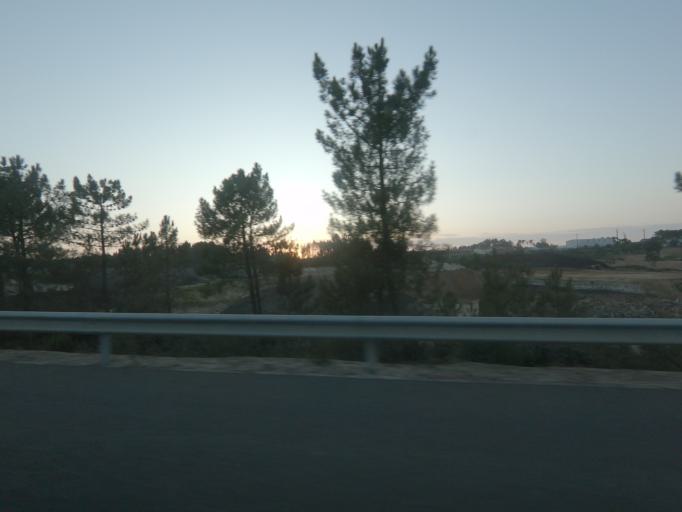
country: PT
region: Leiria
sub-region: Pombal
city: Pombal
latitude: 39.9058
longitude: -8.6874
